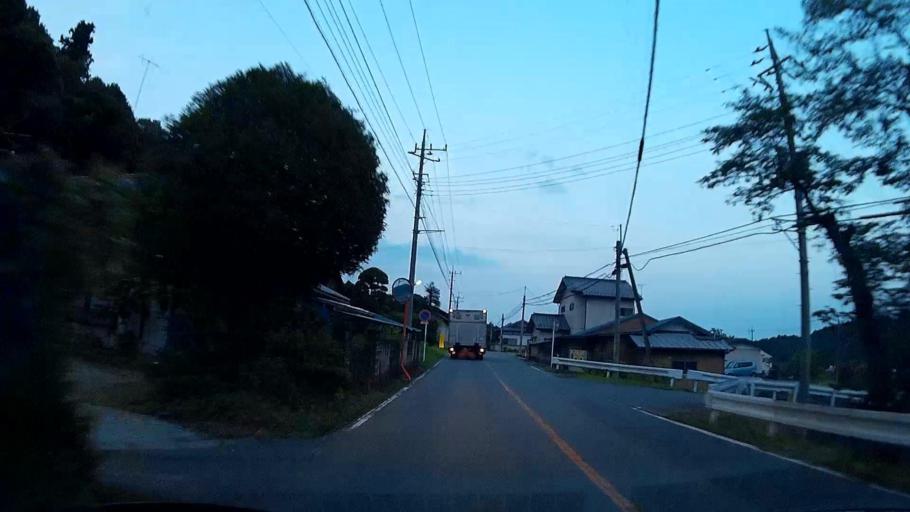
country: JP
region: Gunma
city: Annaka
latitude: 36.3839
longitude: 138.8699
